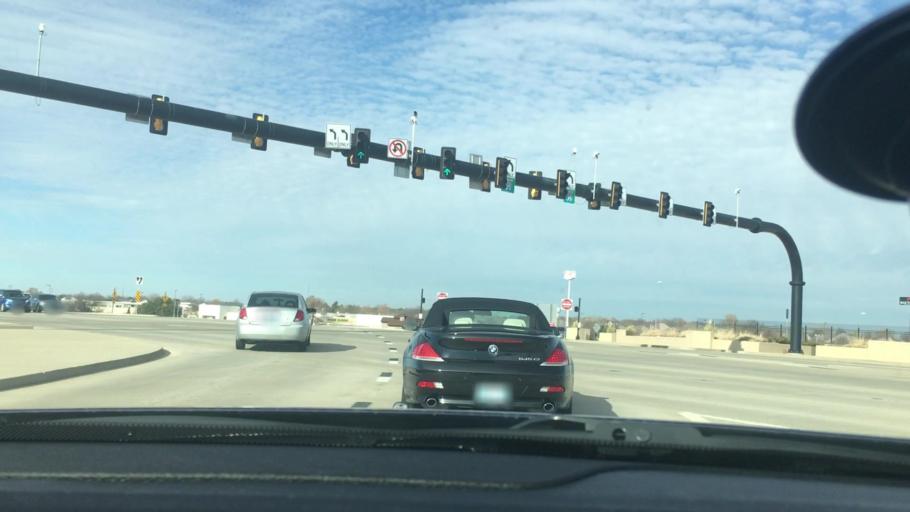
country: US
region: Oklahoma
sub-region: Cleveland County
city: Norman
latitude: 35.2178
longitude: -97.4852
